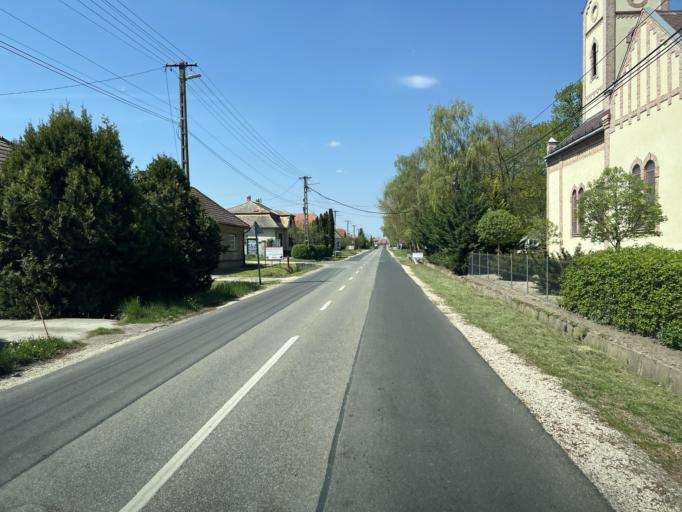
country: HU
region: Pest
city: Kakucs
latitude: 47.2409
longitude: 19.3660
